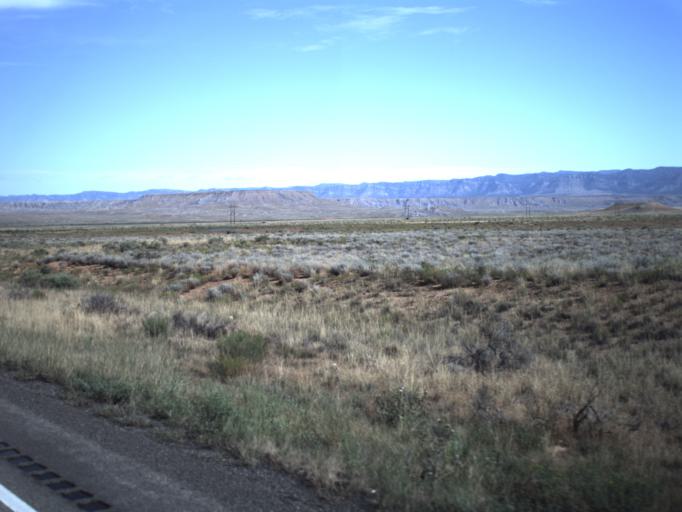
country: US
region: Utah
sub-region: Carbon County
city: East Carbon City
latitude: 39.4425
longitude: -110.4659
